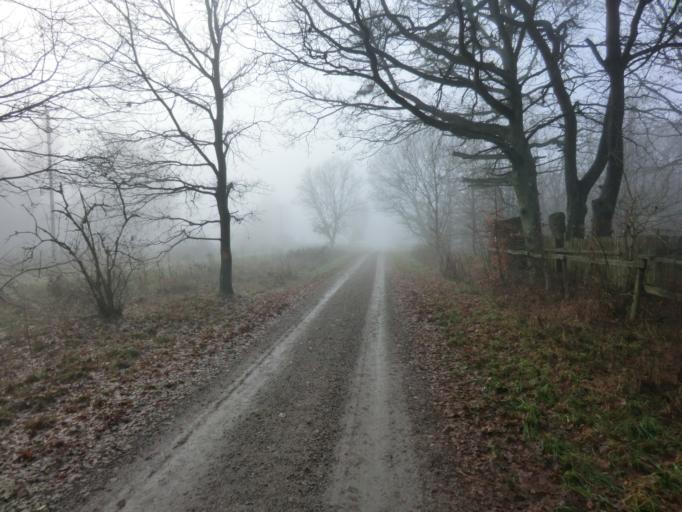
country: SE
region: Skane
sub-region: Lunds Kommun
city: Veberod
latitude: 55.6922
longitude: 13.4969
